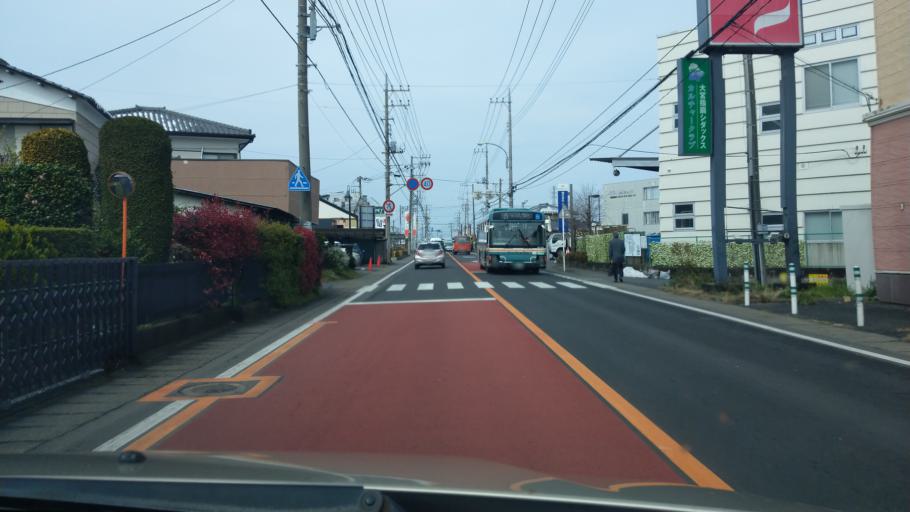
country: JP
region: Saitama
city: Yono
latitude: 35.9121
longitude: 139.5835
